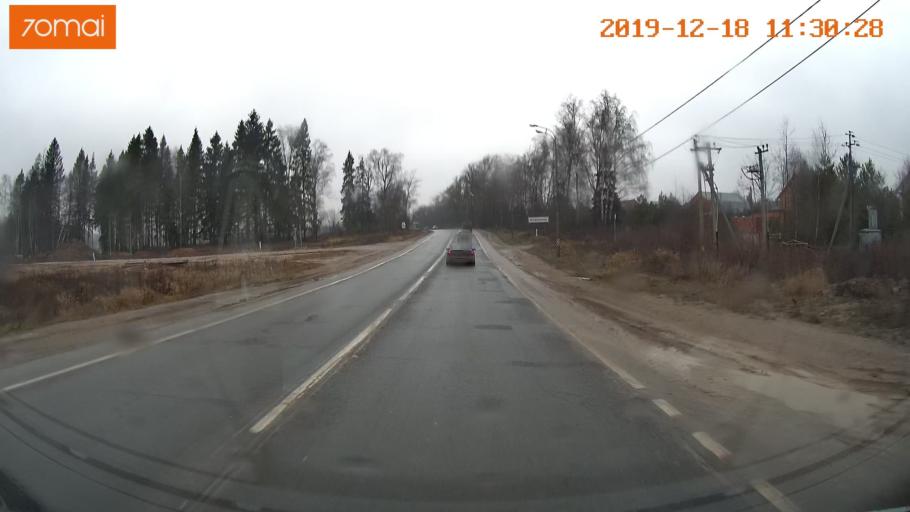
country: RU
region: Moskovskaya
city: Bol'shiye Vyazemy
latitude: 55.6578
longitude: 36.9681
